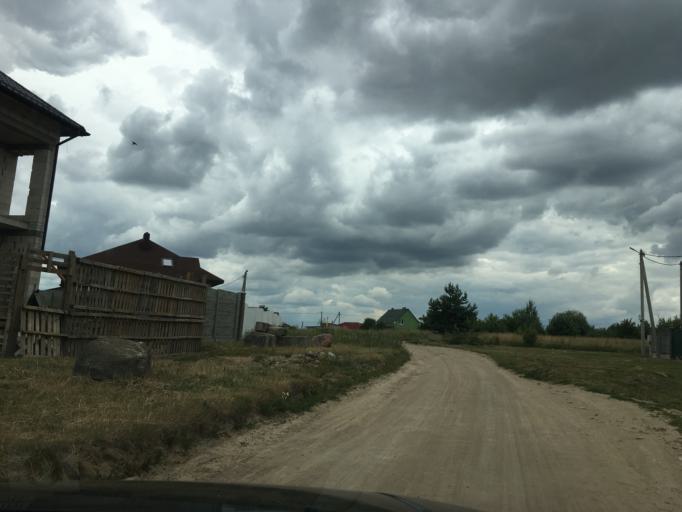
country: BY
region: Grodnenskaya
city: Hrodna
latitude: 53.6185
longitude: 23.8296
